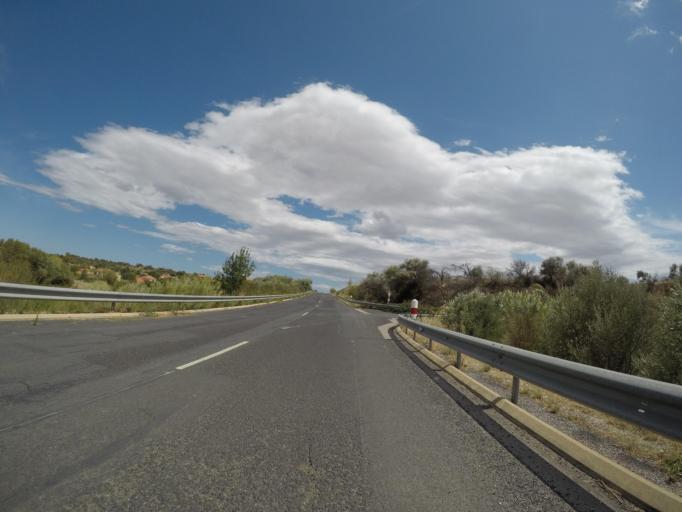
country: FR
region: Languedoc-Roussillon
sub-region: Departement des Pyrenees-Orientales
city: Baixas
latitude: 42.7452
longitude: 2.8078
